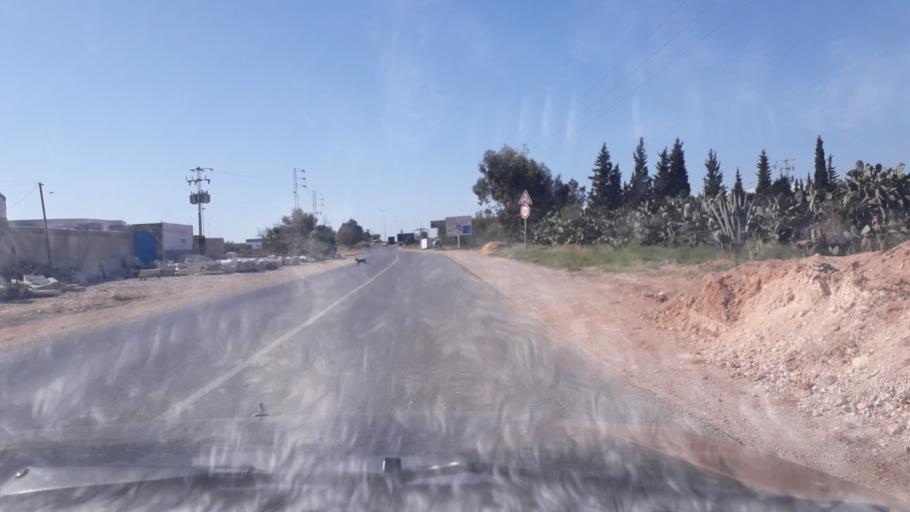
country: TN
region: Safaqis
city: Al Qarmadah
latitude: 34.8593
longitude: 10.7593
